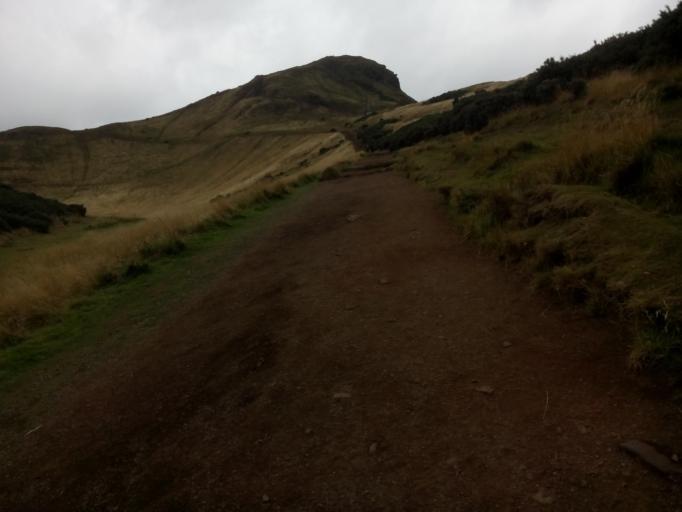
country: GB
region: Scotland
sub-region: West Lothian
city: Seafield
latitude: 55.9476
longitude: -3.1613
